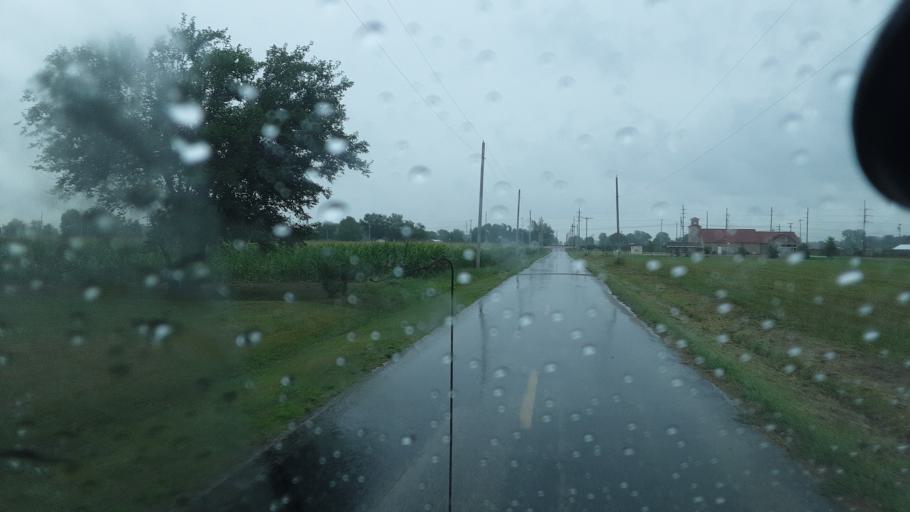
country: US
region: Ohio
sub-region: Williams County
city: Montpelier
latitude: 41.6004
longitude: -84.5605
